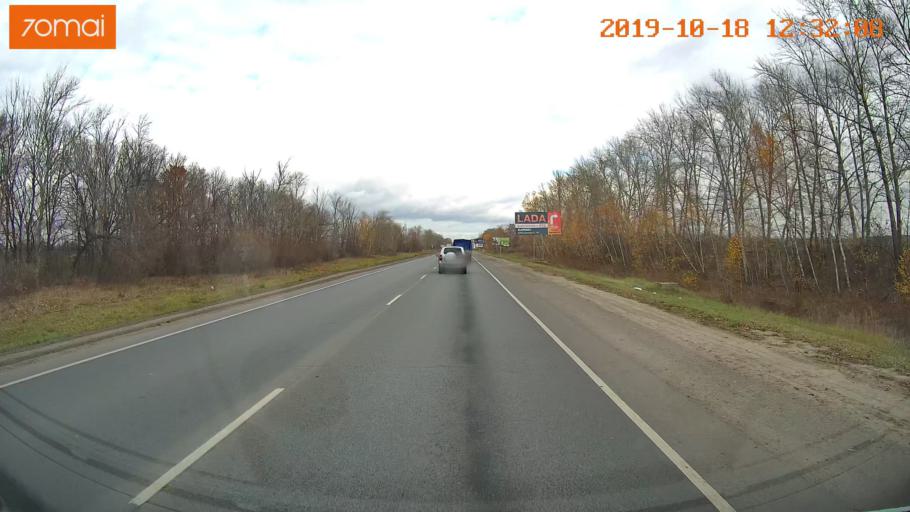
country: RU
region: Rjazan
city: Ryazan'
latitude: 54.5987
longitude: 39.6213
